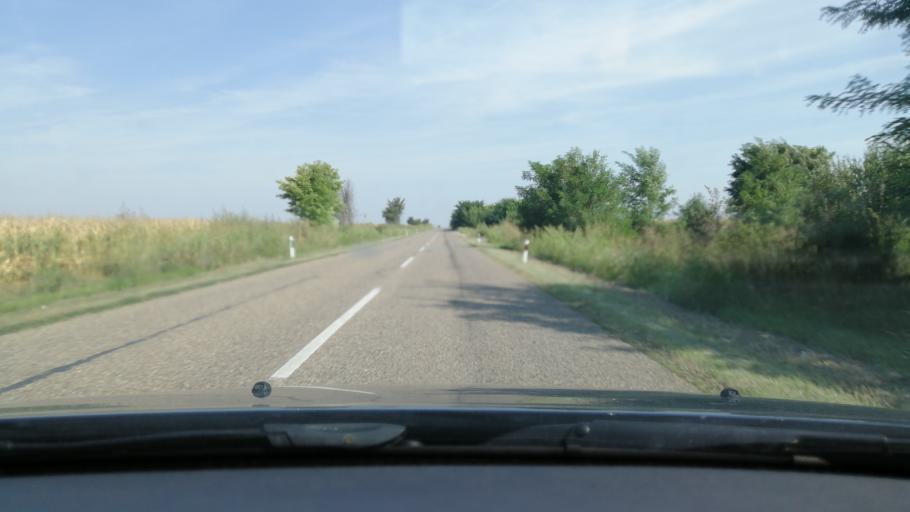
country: RS
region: Autonomna Pokrajina Vojvodina
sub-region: Juznobanatski Okrug
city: Kovacica
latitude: 45.1499
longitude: 20.6168
